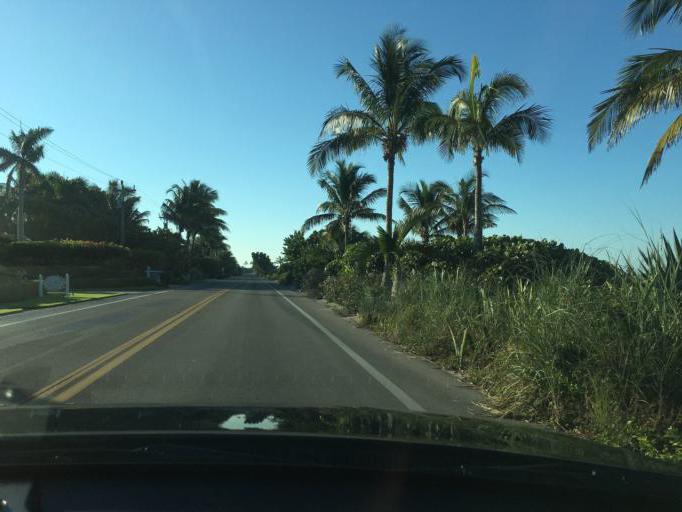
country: US
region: Florida
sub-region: Lee County
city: Saint James City
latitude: 26.5154
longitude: -82.1918
